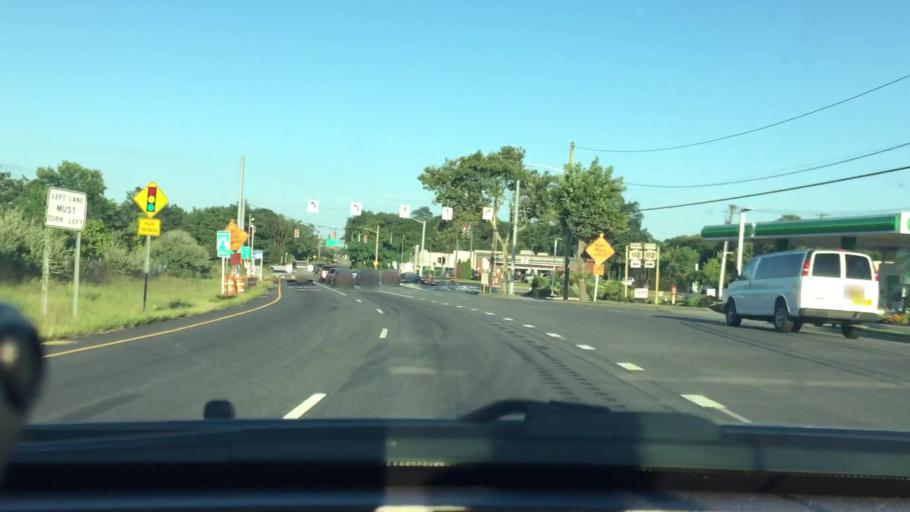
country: US
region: New York
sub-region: Suffolk County
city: Medford
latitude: 40.8230
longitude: -72.9985
